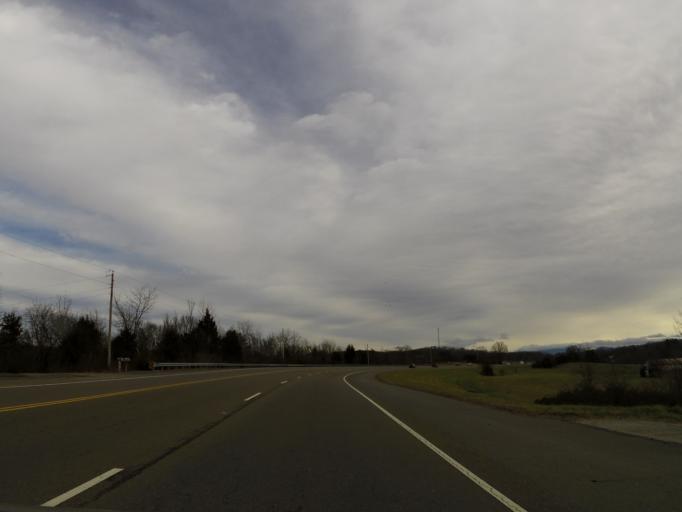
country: US
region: Tennessee
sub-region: Cocke County
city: Newport
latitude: 35.9869
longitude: -83.1535
